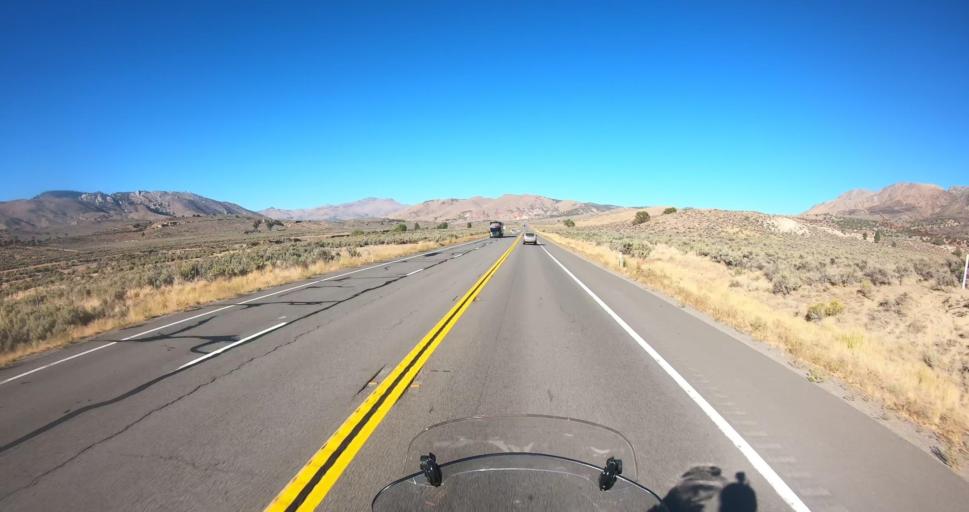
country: US
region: Nevada
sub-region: Washoe County
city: Cold Springs
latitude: 39.8748
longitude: -120.0329
